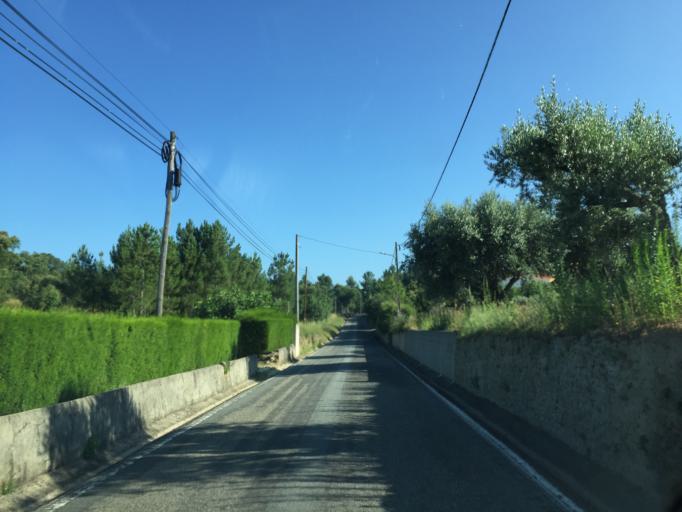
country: PT
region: Santarem
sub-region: Abrantes
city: Alferrarede
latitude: 39.5222
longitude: -8.1385
